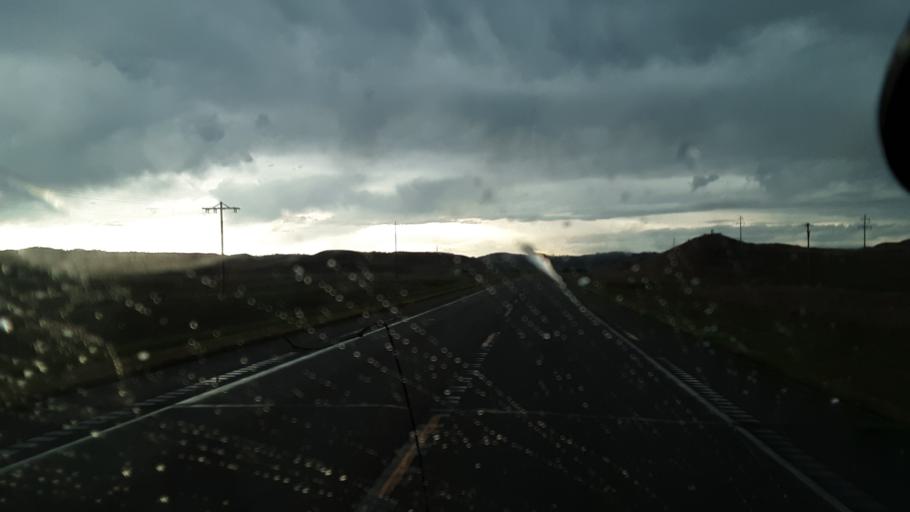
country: US
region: Montana
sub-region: Powder River County
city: Broadus
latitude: 45.5396
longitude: -105.8211
